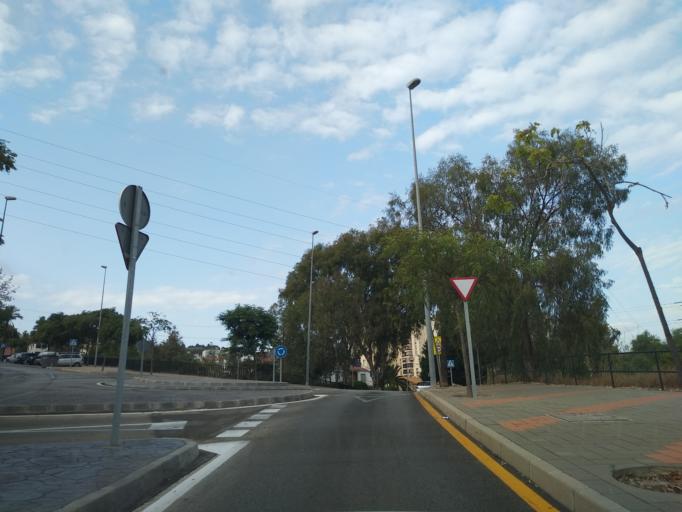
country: ES
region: Andalusia
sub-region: Provincia de Malaga
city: Malaga
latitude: 36.7294
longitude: -4.4741
